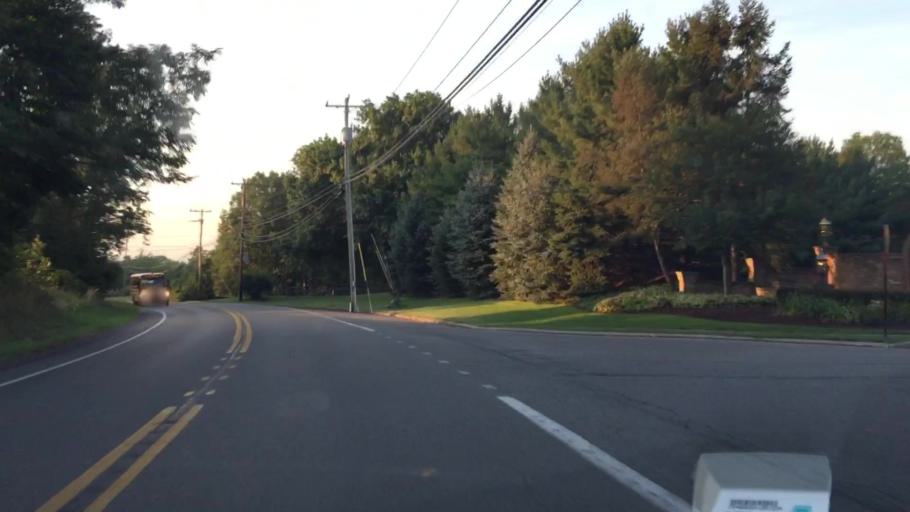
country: US
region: Pennsylvania
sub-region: Allegheny County
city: Franklin Park
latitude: 40.5780
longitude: -80.1083
